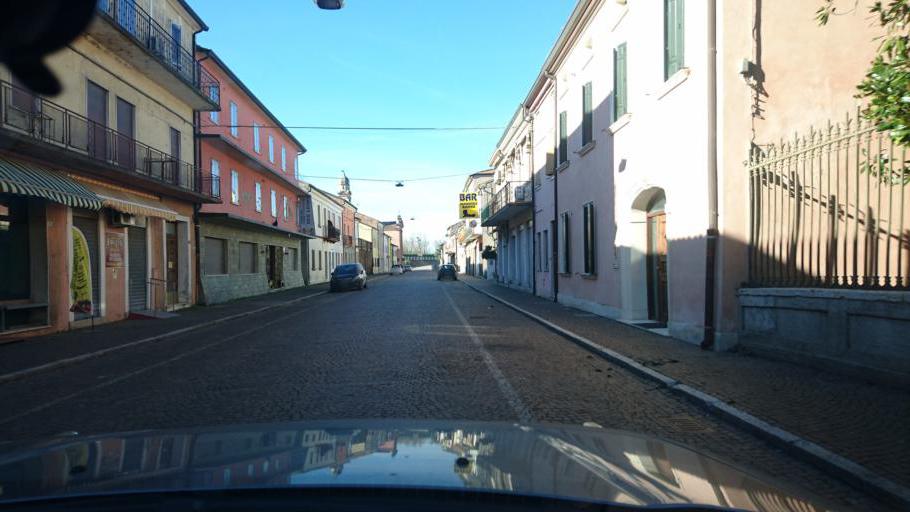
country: IT
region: Veneto
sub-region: Provincia di Rovigo
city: Ariano
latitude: 44.9456
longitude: 12.1204
